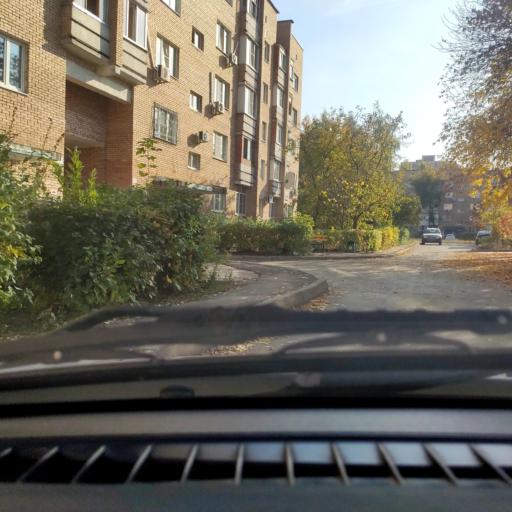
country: RU
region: Samara
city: Tol'yatti
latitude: 53.5172
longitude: 49.2972
